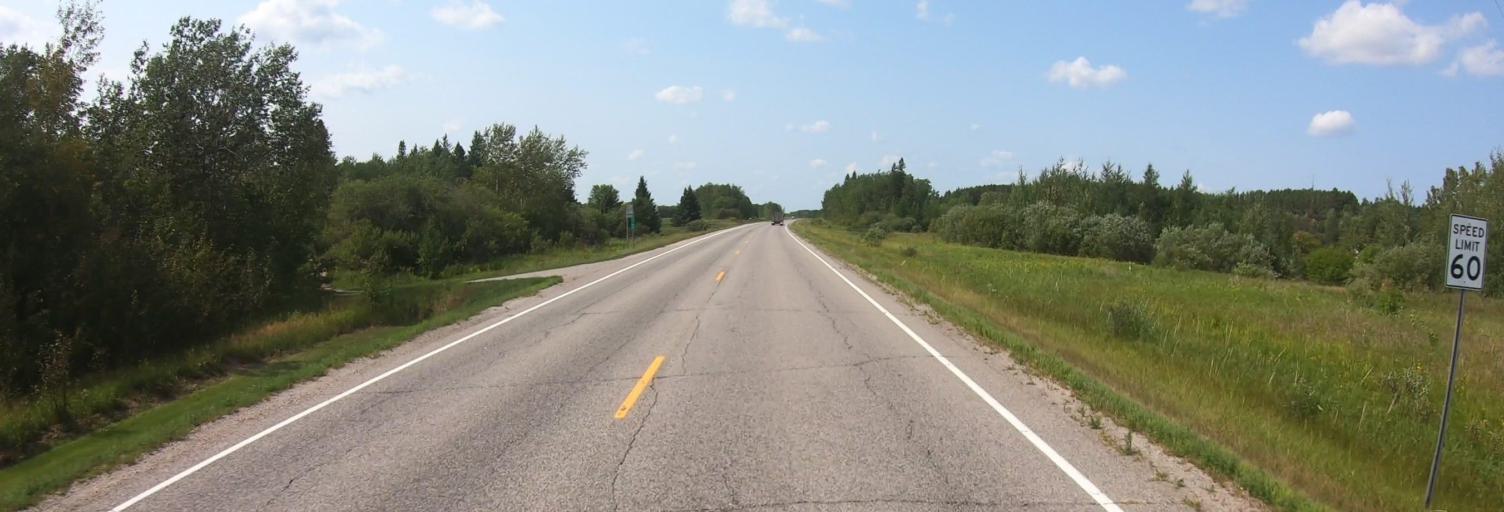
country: US
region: Minnesota
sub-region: Roseau County
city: Warroad
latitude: 48.8036
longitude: -95.1014
